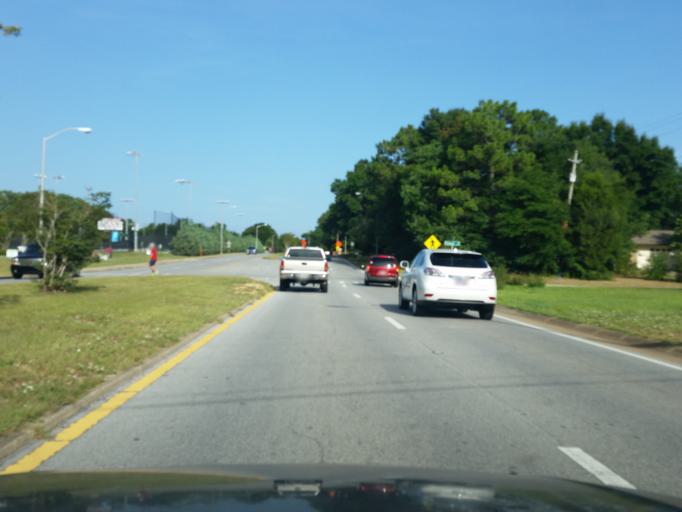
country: US
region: Florida
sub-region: Escambia County
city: Goulding
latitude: 30.4655
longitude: -87.1971
